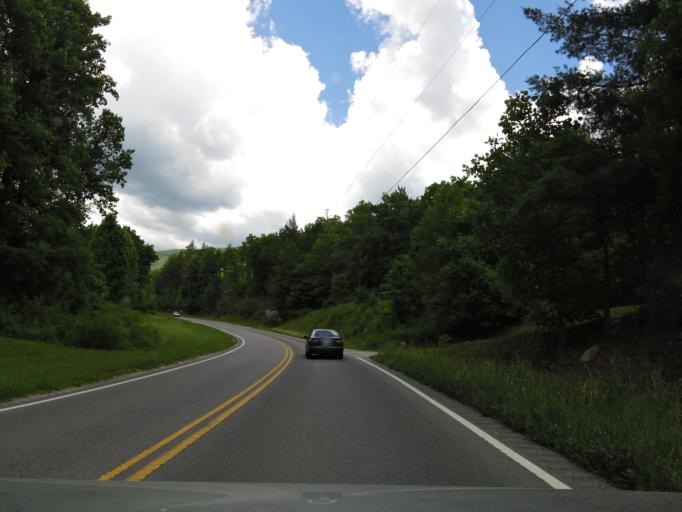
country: US
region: North Carolina
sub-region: Graham County
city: Robbinsville
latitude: 35.2704
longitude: -83.7312
